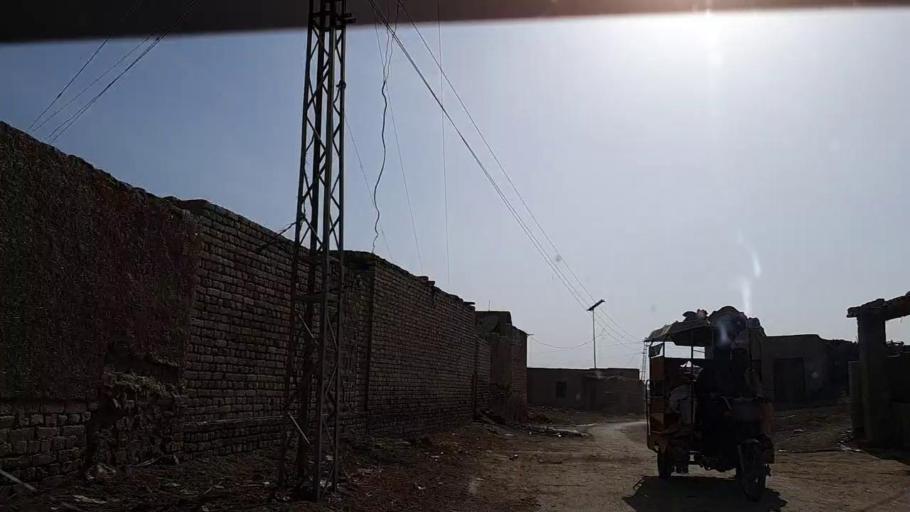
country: PK
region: Sindh
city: Phulji
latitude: 26.9908
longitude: 67.6513
